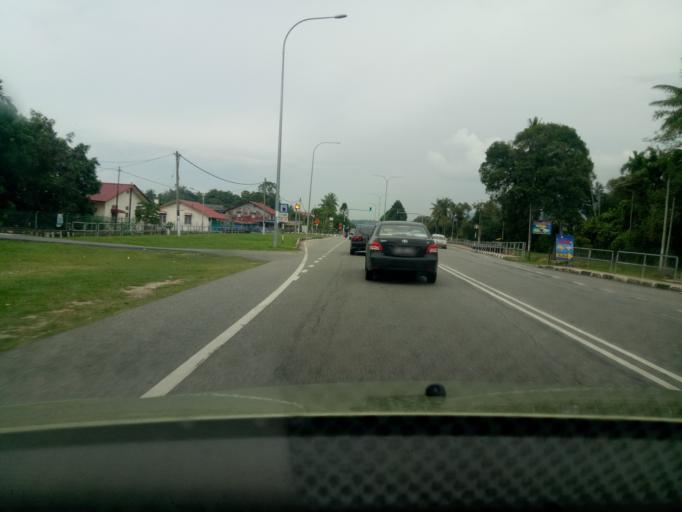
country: MY
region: Kedah
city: Gurun
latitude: 5.8648
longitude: 100.4547
